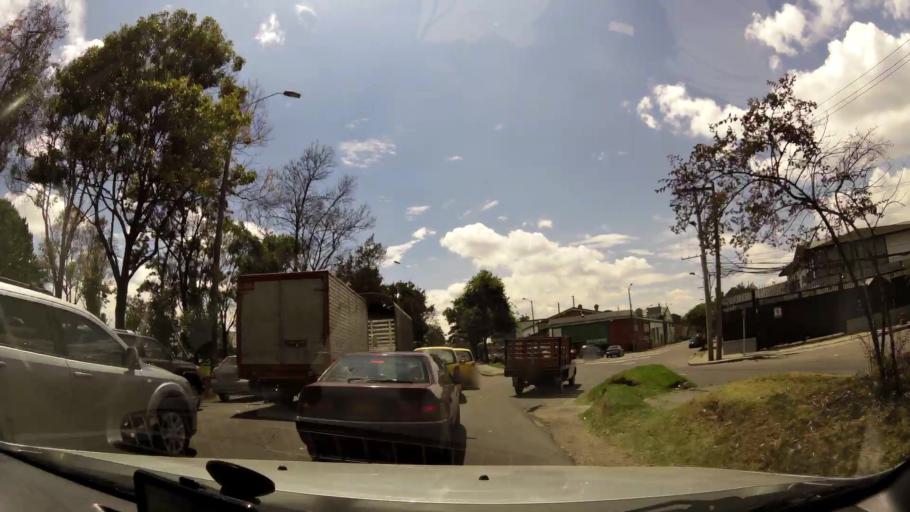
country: CO
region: Bogota D.C.
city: Bogota
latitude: 4.6267
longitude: -74.0975
